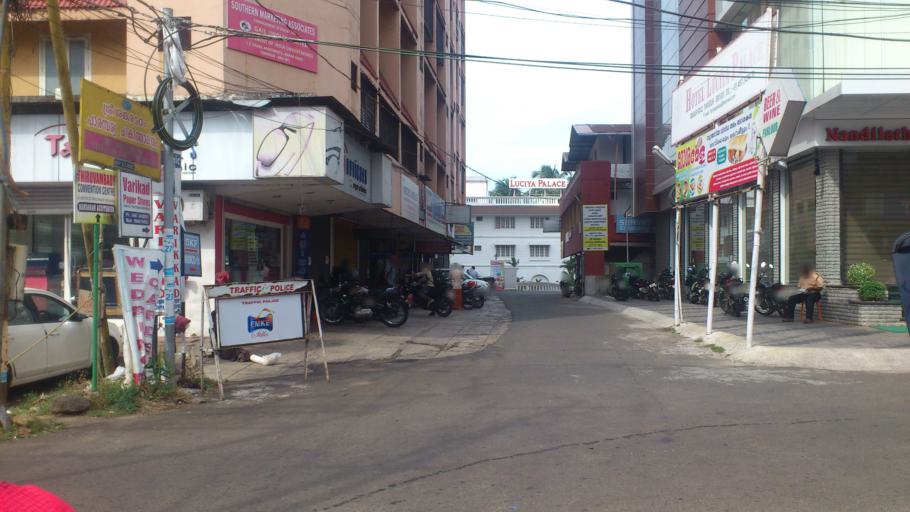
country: IN
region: Kerala
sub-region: Thrissur District
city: Trichur
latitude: 10.5223
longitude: 76.2121
